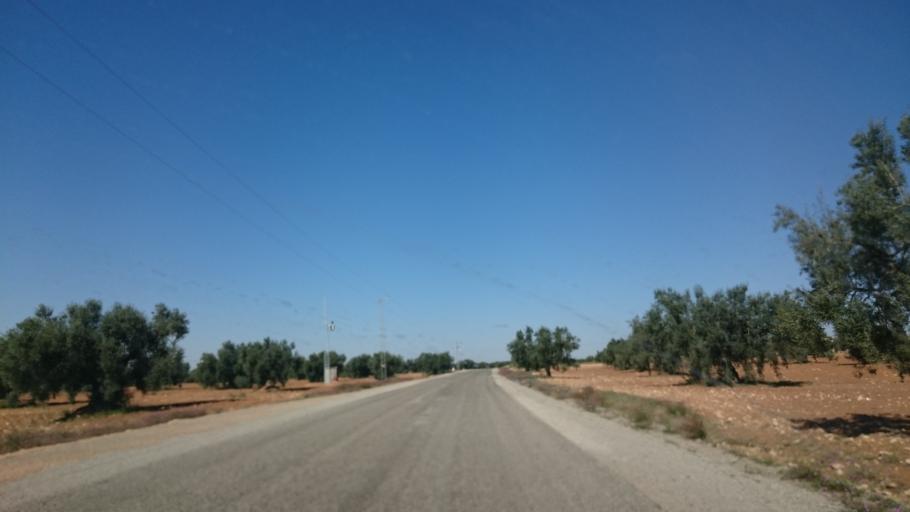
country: TN
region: Safaqis
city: Sfax
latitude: 34.8571
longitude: 10.4372
